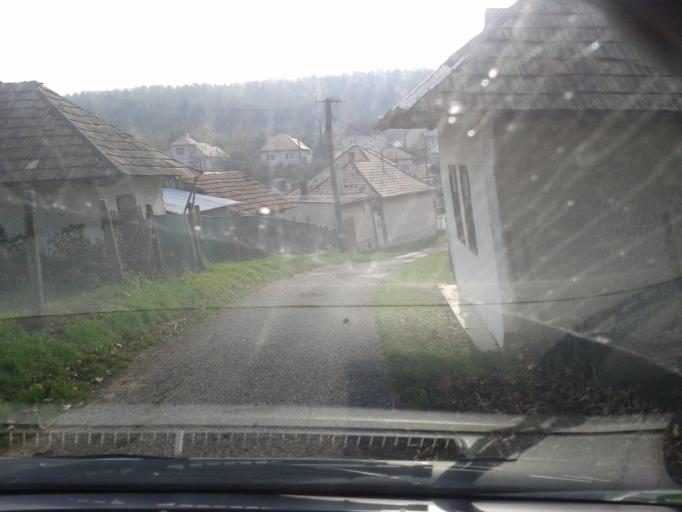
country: SK
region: Nitriansky
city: Svodin
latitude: 48.0409
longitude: 18.4754
